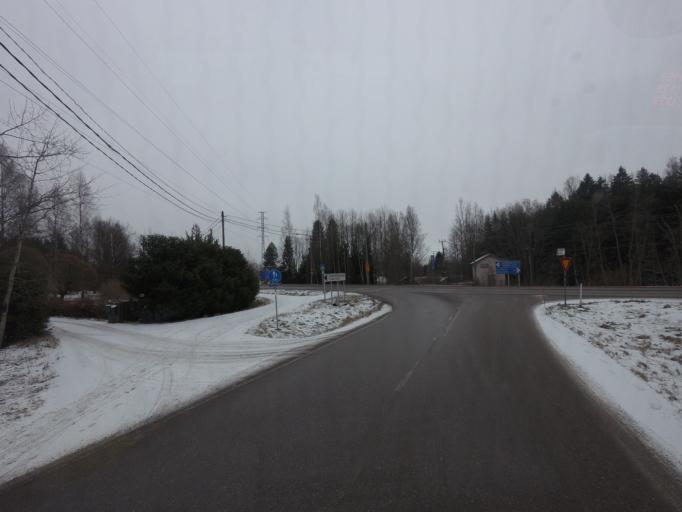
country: FI
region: Uusimaa
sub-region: Helsinki
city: Espoo
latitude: 60.1916
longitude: 24.5708
